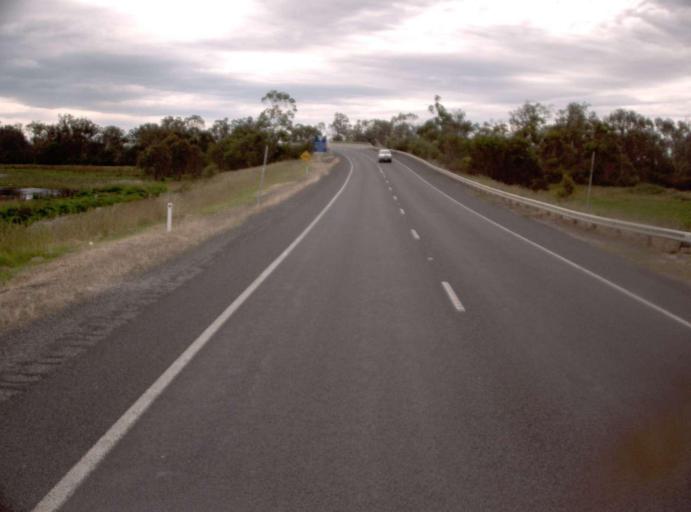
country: AU
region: Victoria
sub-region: Wellington
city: Sale
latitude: -38.1456
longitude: 147.0814
